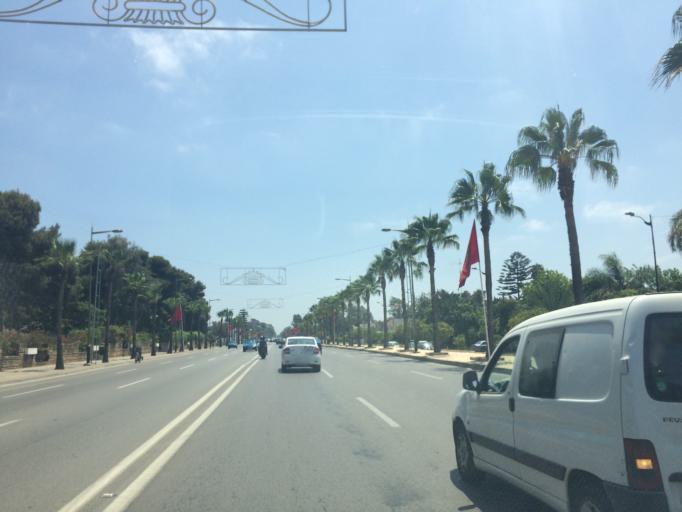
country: MA
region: Rabat-Sale-Zemmour-Zaer
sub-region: Rabat
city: Rabat
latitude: 33.9921
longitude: -6.8275
